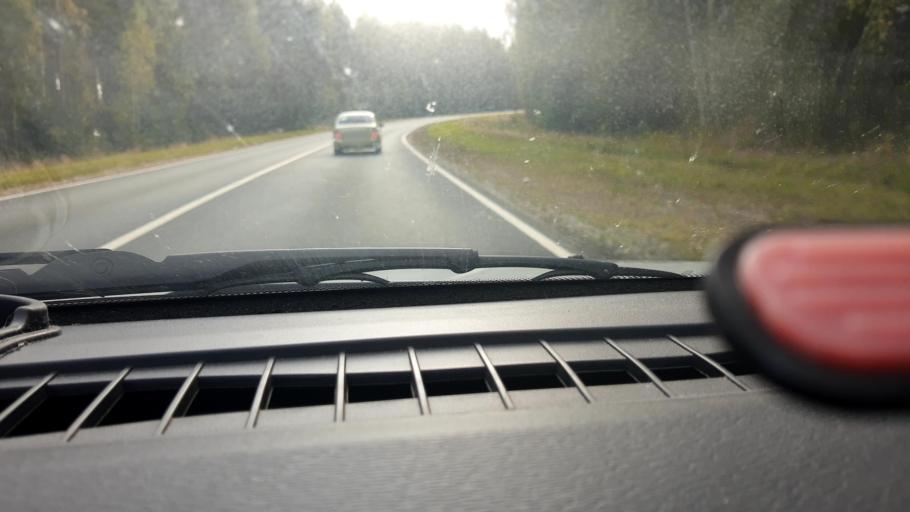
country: RU
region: Nizjnij Novgorod
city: Krasnyye Baki
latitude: 57.2176
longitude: 45.4833
